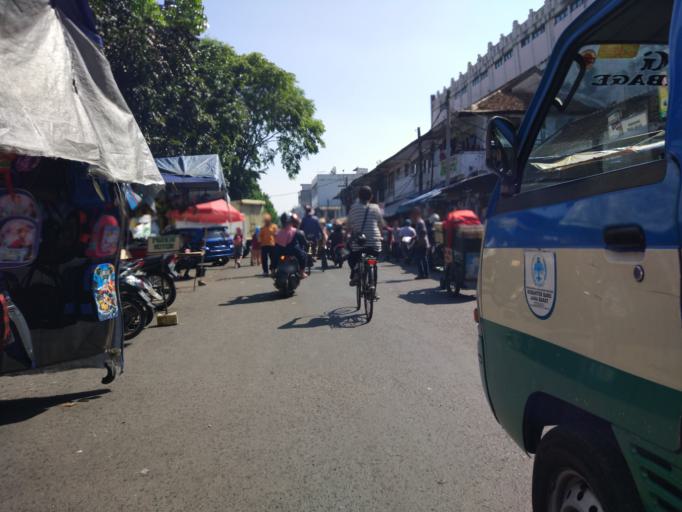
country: ID
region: West Java
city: Bandung
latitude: -6.9334
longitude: 107.6024
